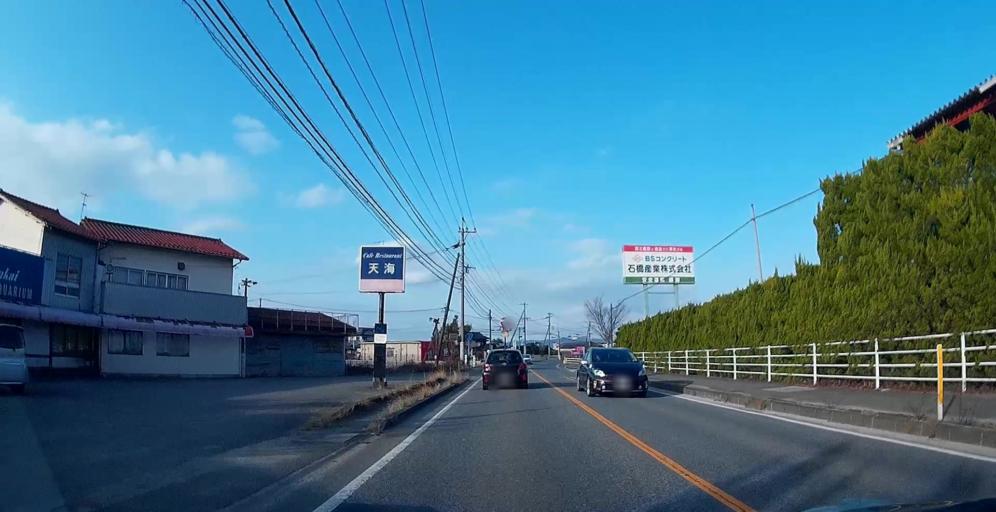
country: JP
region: Kumamoto
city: Matsubase
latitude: 32.6028
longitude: 130.7022
